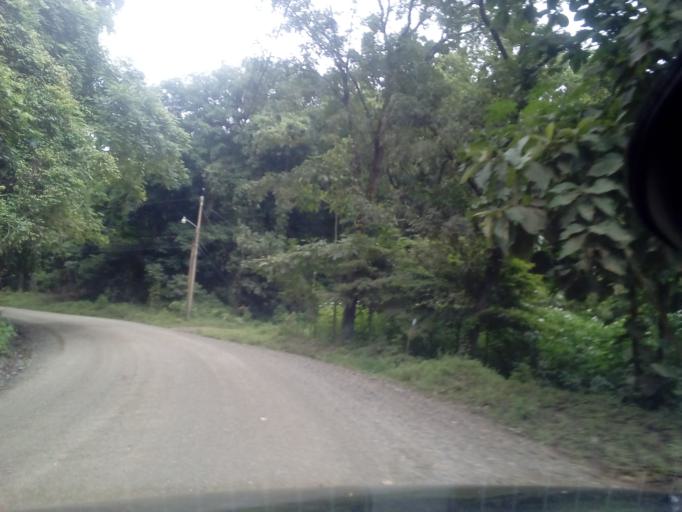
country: CR
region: Guanacaste
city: Samara
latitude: 9.9145
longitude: -85.5550
